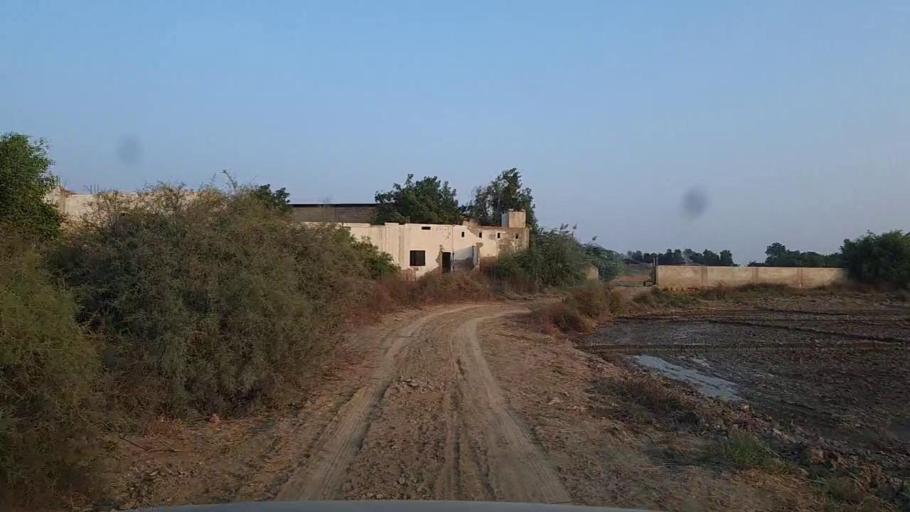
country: PK
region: Sindh
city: Mirpur Sakro
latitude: 24.6130
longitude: 67.5933
